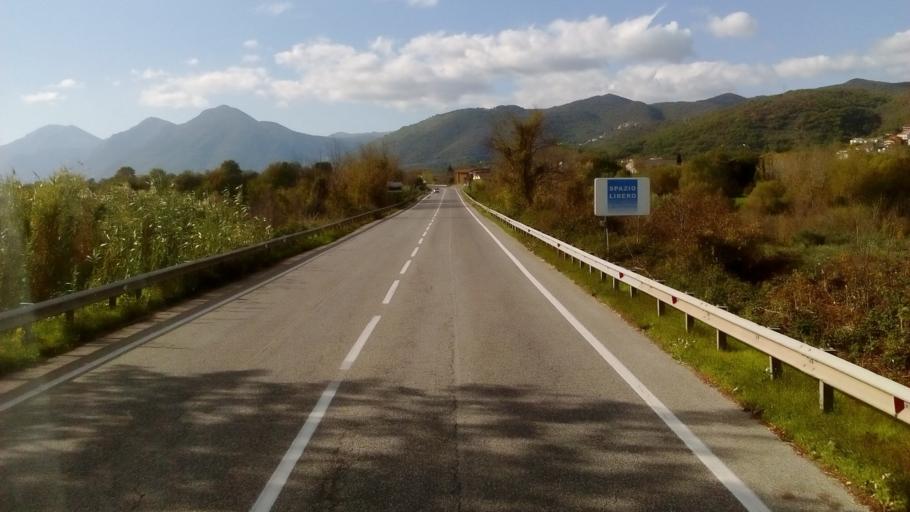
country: IT
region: Molise
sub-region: Provincia di Isernia
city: Taverna Ravindola
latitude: 41.5181
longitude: 14.1341
